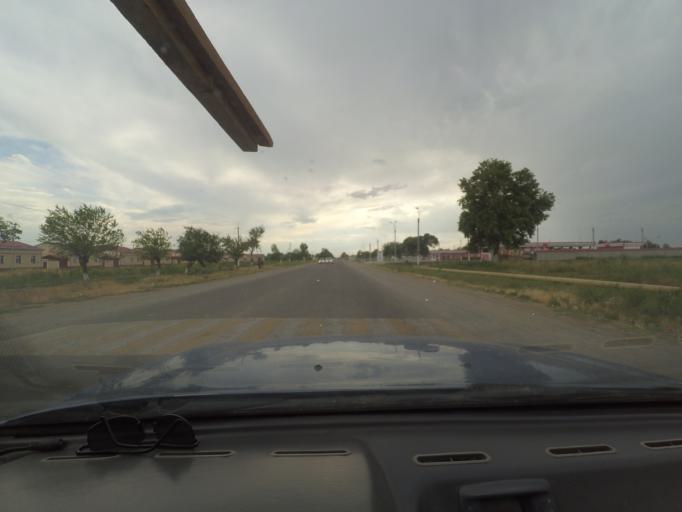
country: UZ
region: Sirdaryo
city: Guliston
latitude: 40.4927
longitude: 68.8251
